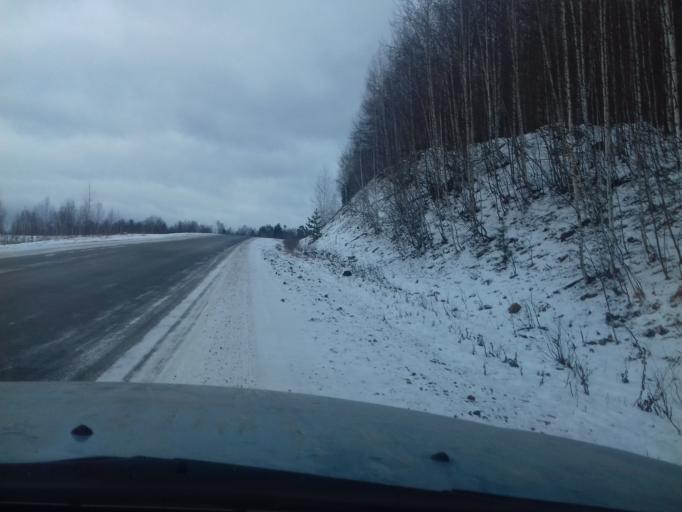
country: RU
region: Bashkortostan
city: Starosubkhangulovo
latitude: 53.1566
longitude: 57.4094
